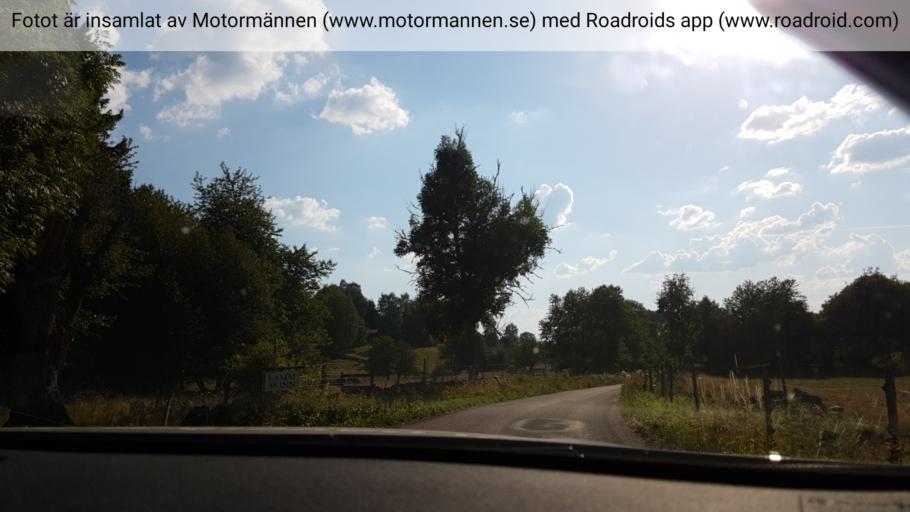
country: SE
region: Vaestra Goetaland
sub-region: Skovde Kommun
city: Skoevde
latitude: 58.4523
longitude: 13.7276
